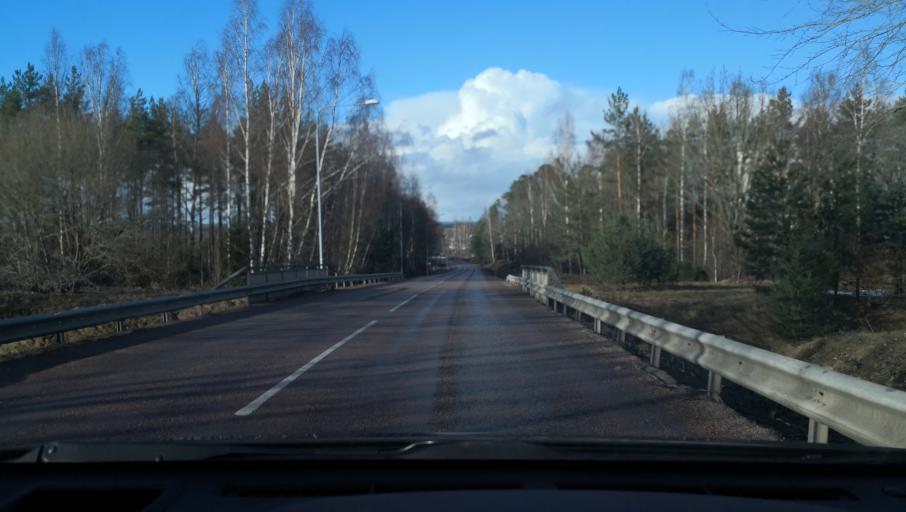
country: SE
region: Vaestmanland
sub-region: Arboga Kommun
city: Arboga
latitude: 59.3817
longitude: 15.8390
